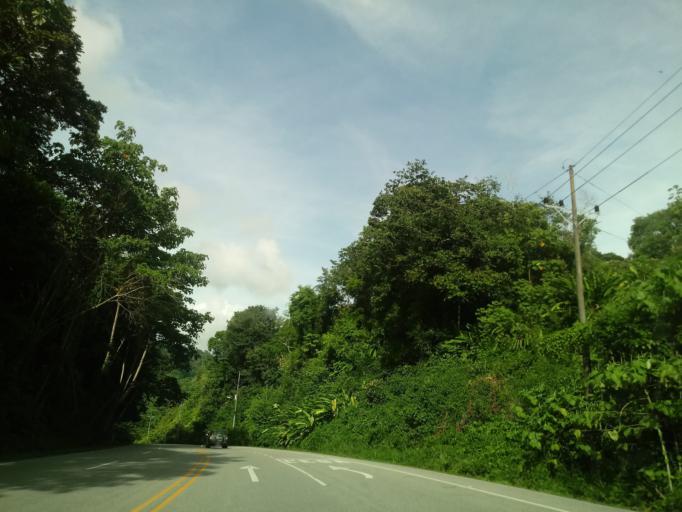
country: CR
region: San Jose
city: Daniel Flores
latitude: 9.1998
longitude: -83.7885
